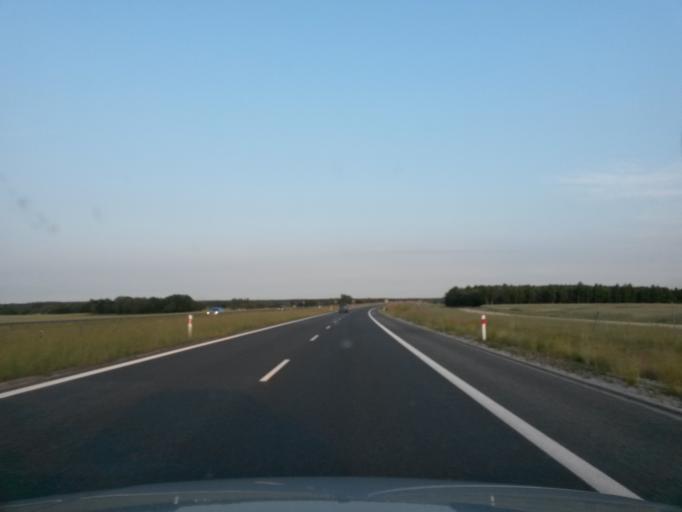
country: PL
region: Lodz Voivodeship
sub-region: Powiat wieruszowski
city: Wieruszow
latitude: 51.3324
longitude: 18.1436
